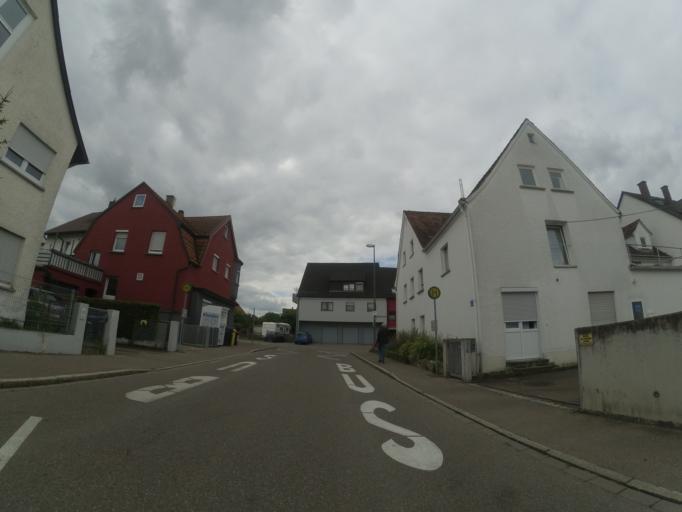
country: DE
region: Bavaria
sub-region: Swabia
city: Neu-Ulm
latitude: 48.4038
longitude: 10.0209
